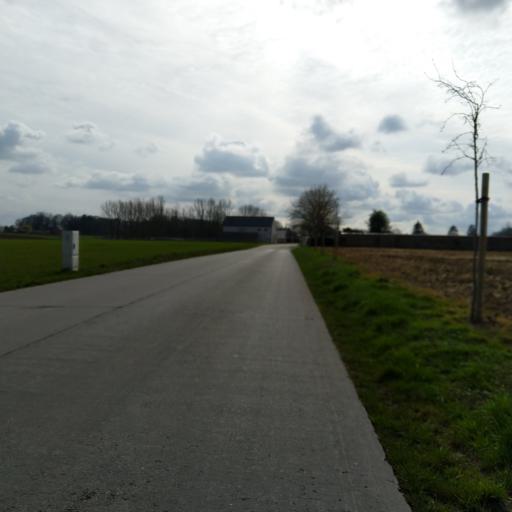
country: BE
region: Wallonia
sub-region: Province du Hainaut
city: Soignies
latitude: 50.5220
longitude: 4.0552
